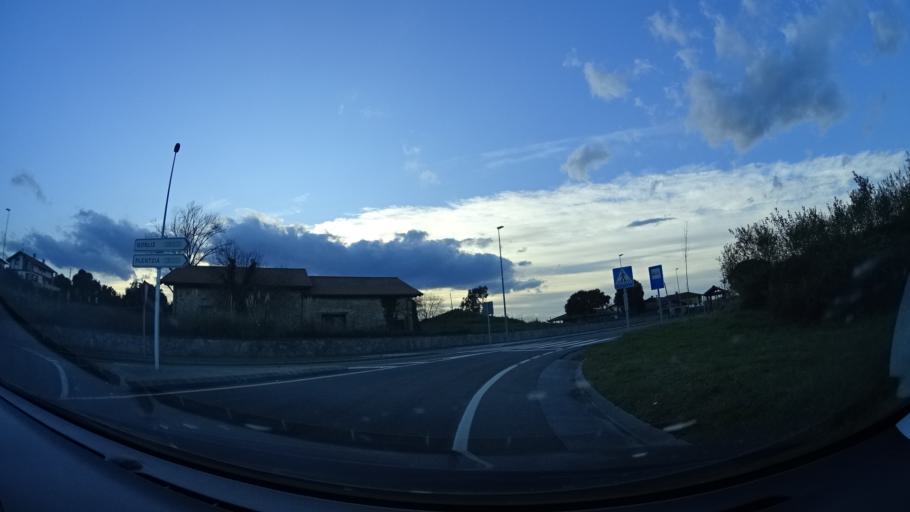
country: ES
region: Basque Country
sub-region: Bizkaia
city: Elexalde
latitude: 43.3976
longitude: -2.9070
